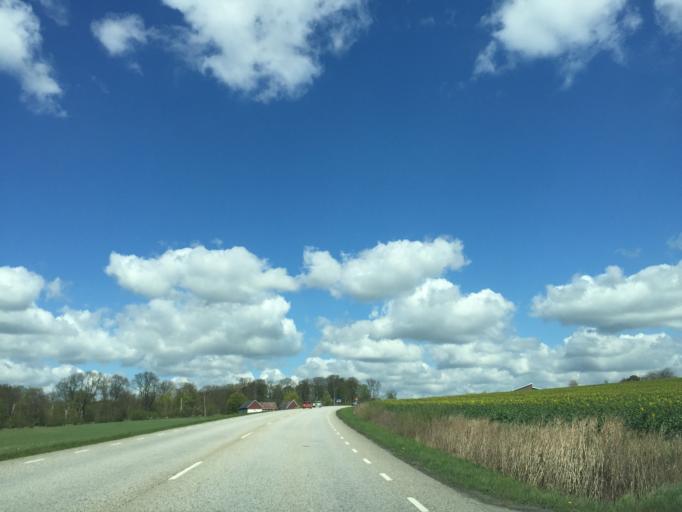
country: SE
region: Skane
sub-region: Lunds Kommun
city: Genarp
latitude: 55.6685
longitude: 13.3331
